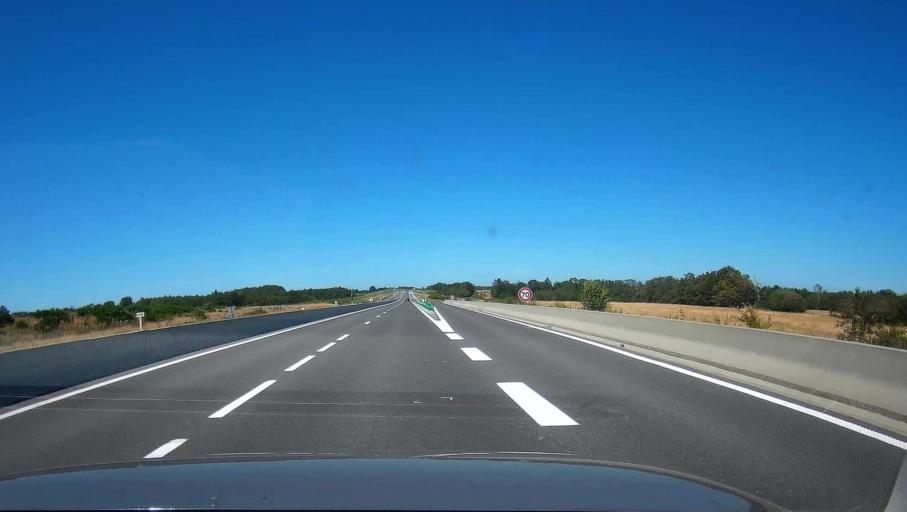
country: FR
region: Champagne-Ardenne
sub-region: Departement des Ardennes
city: Rocroi
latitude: 49.8991
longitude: 4.5213
